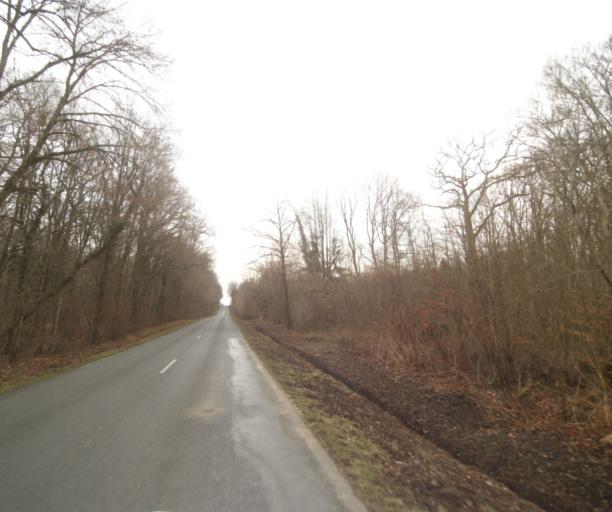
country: FR
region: Champagne-Ardenne
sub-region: Departement de la Haute-Marne
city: Villiers-en-Lieu
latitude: 48.7189
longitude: 4.8784
